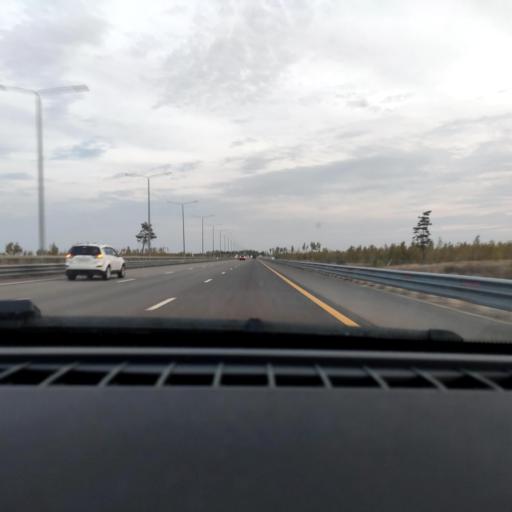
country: RU
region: Voronezj
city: Somovo
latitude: 51.7717
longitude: 39.3021
